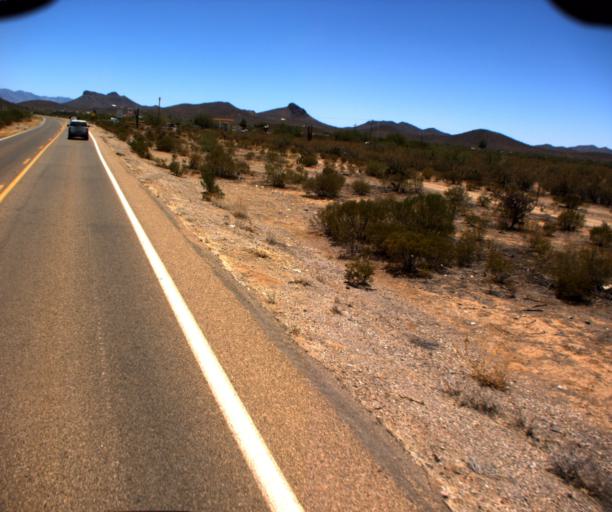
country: US
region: Arizona
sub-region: Pima County
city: Sells
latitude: 31.9266
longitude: -111.9013
